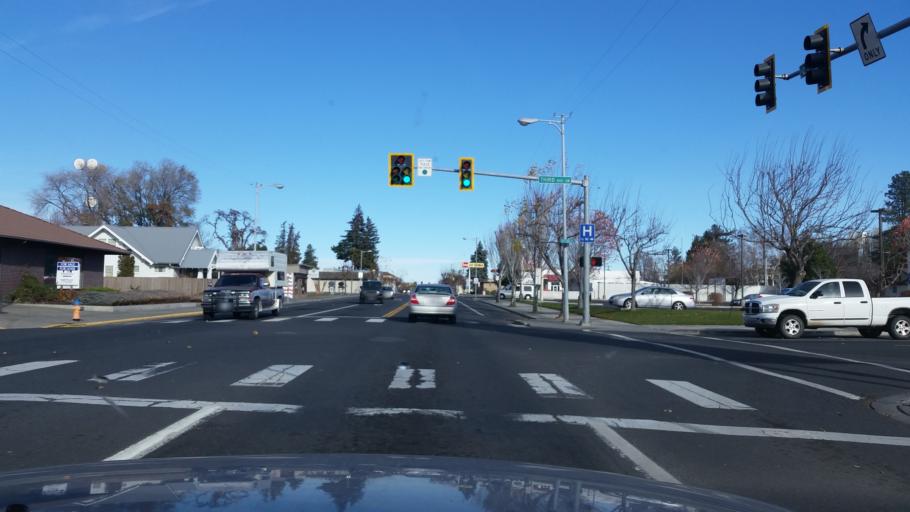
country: US
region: Washington
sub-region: Grant County
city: Ephrata
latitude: 47.3173
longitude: -119.5540
